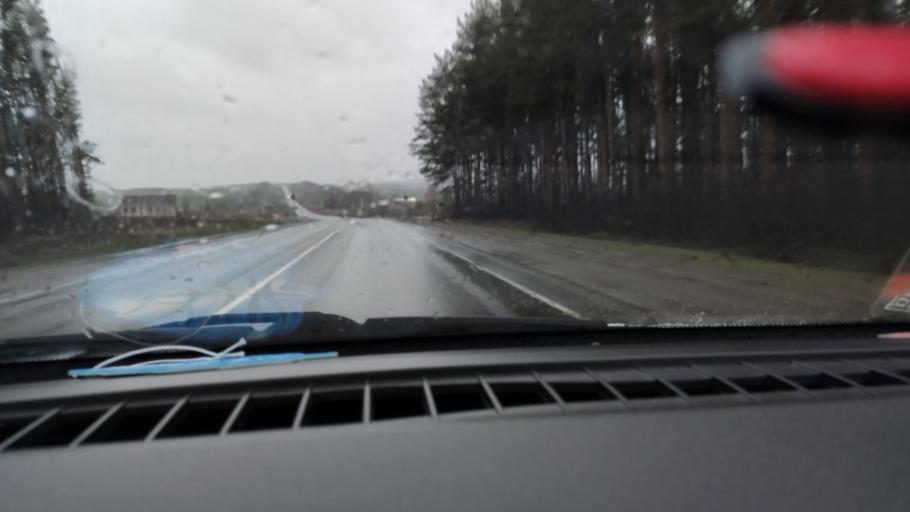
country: RU
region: Tatarstan
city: Mendeleyevsk
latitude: 55.9402
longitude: 52.2904
